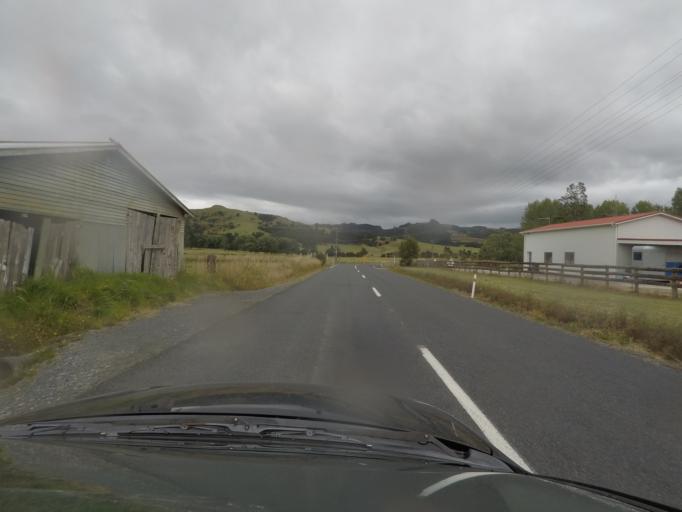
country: NZ
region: Auckland
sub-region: Auckland
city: Warkworth
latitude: -36.2855
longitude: 174.6636
